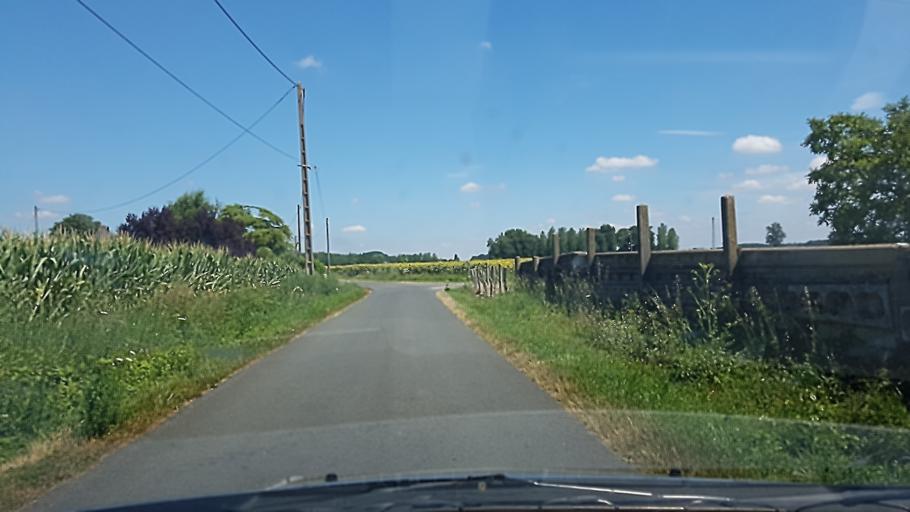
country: FR
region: Pays de la Loire
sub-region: Departement de Maine-et-Loire
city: Le Plessis-Grammoire
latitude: 47.5117
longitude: -0.4091
